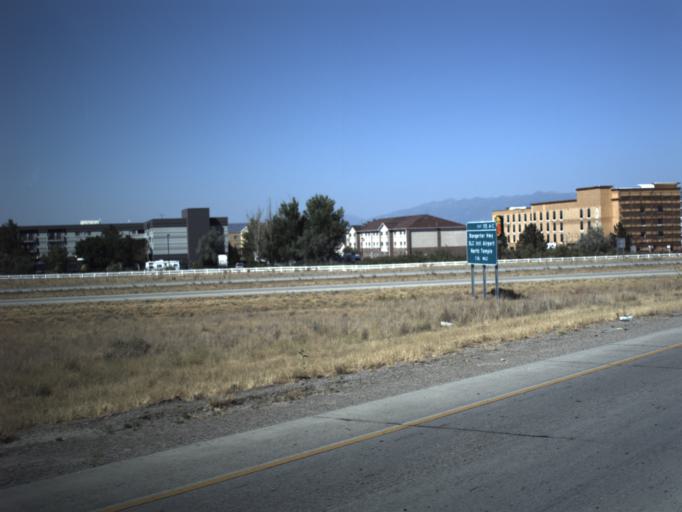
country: US
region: Utah
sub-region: Salt Lake County
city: West Valley City
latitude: 40.7701
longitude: -112.0215
